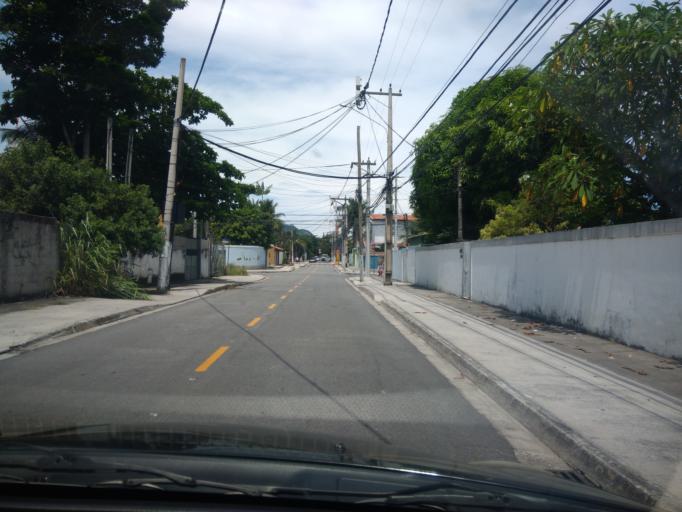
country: BR
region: Rio de Janeiro
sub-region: Niteroi
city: Niteroi
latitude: -22.9333
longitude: -43.0702
